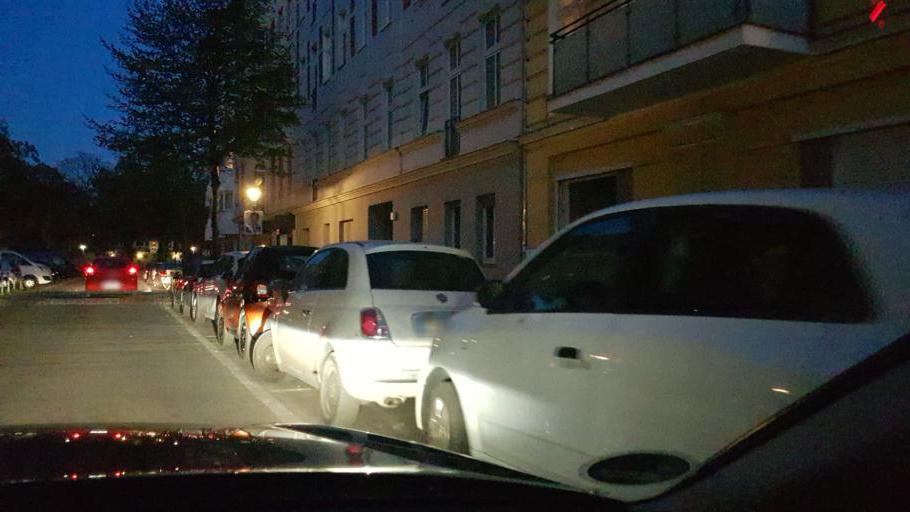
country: DE
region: Berlin
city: Moabit
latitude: 52.5255
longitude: 13.3338
